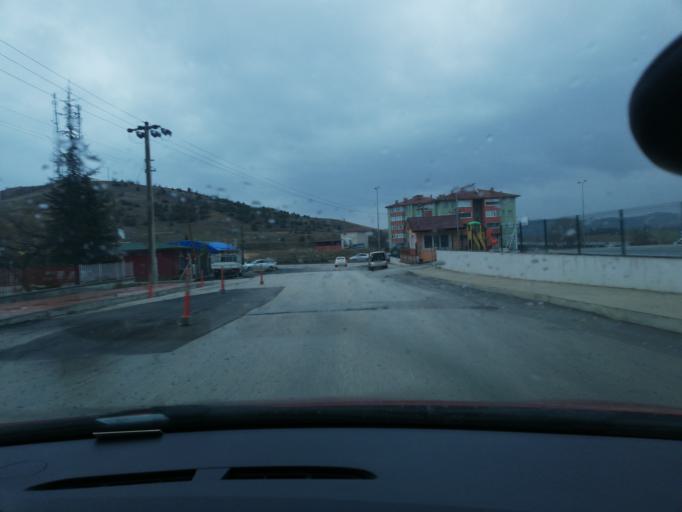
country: TR
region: Kastamonu
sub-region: Cide
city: Kastamonu
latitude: 41.4242
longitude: 33.8007
